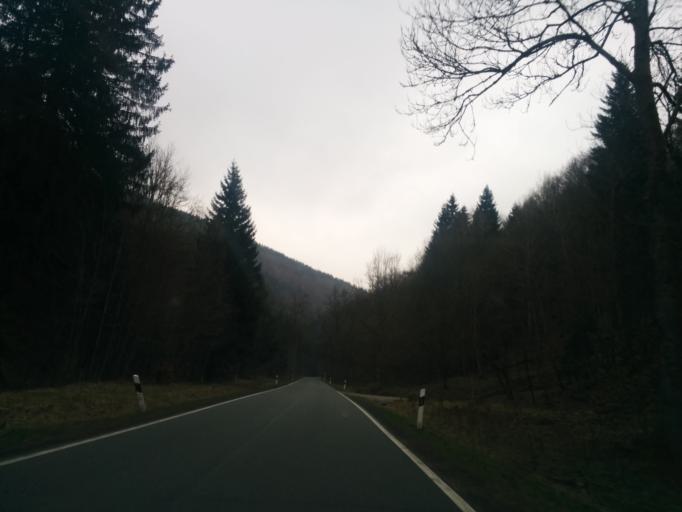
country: DE
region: Lower Saxony
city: Sankt Andreasberg
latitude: 51.6729
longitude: 10.5031
